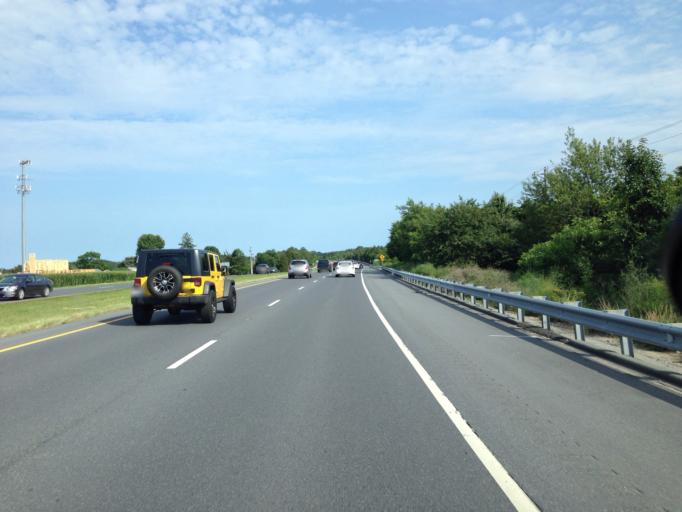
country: US
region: Delaware
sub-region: Sussex County
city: Milton
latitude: 38.7952
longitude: -75.2579
